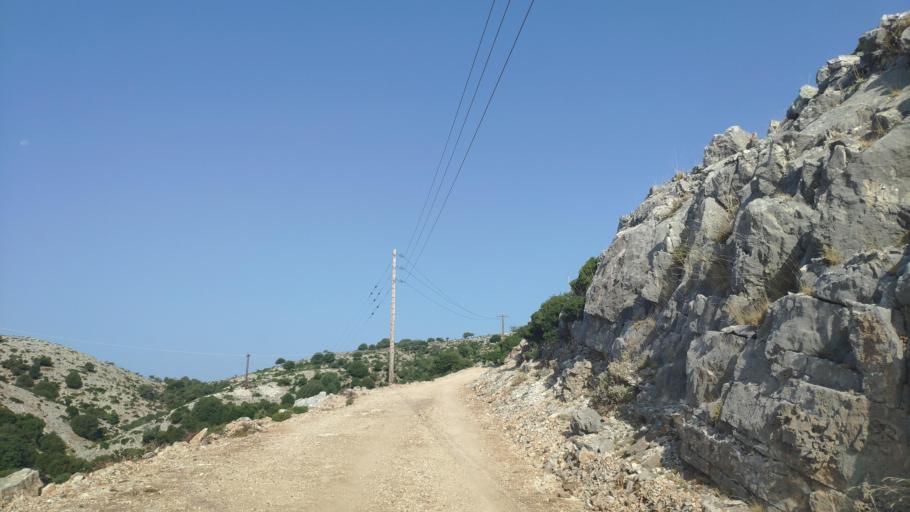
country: GR
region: West Greece
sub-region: Nomos Aitolias kai Akarnanias
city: Monastirakion
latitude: 38.8240
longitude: 20.9797
